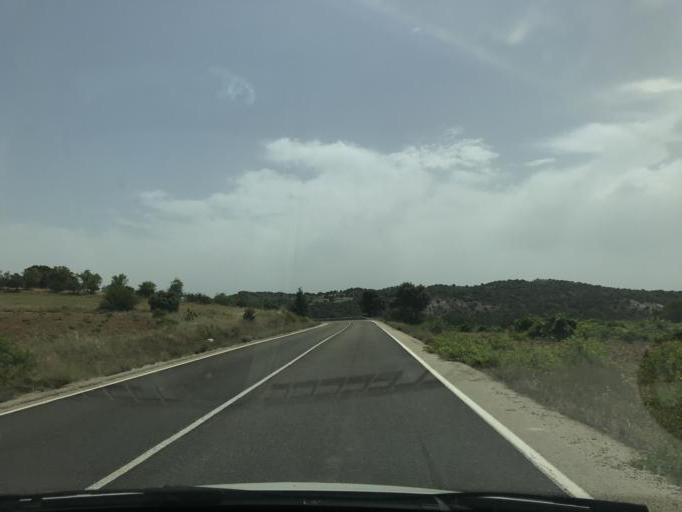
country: ES
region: Castille-La Mancha
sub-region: Provincia de Cuenca
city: Albalate de las Nogueras
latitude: 40.3944
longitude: -2.2596
